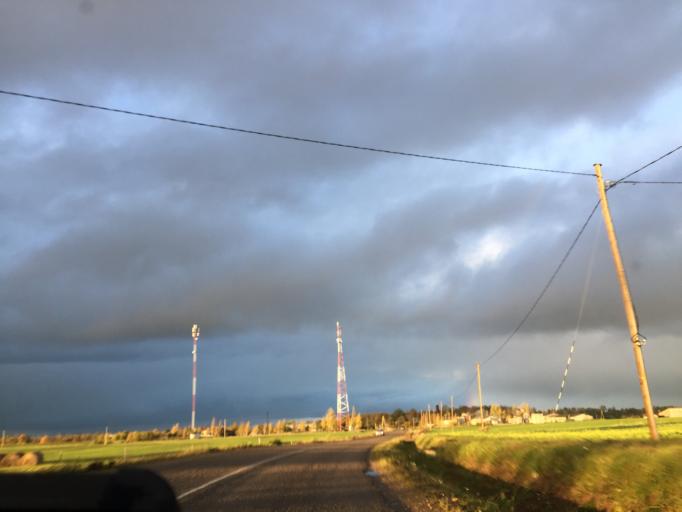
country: LV
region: Talsu Rajons
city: Sabile
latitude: 56.9413
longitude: 22.3966
